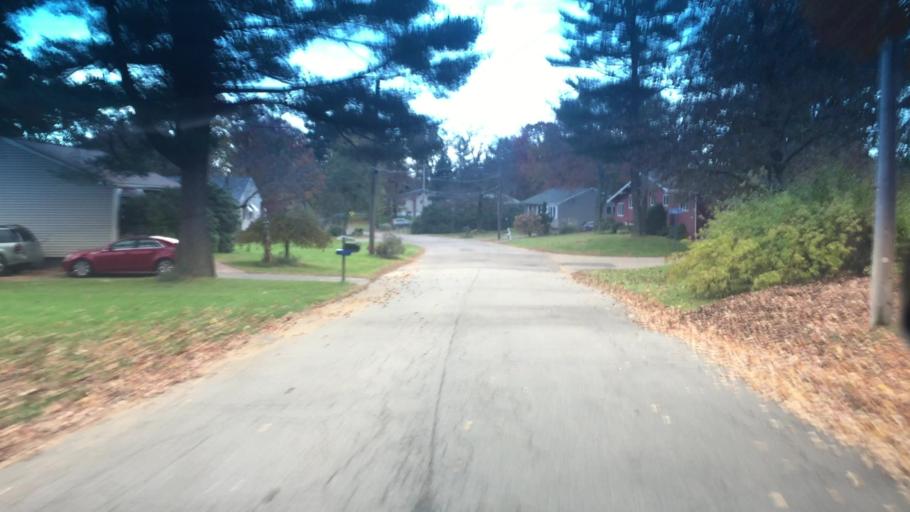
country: US
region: Massachusetts
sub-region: Norfolk County
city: Medway
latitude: 42.1551
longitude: -71.4051
